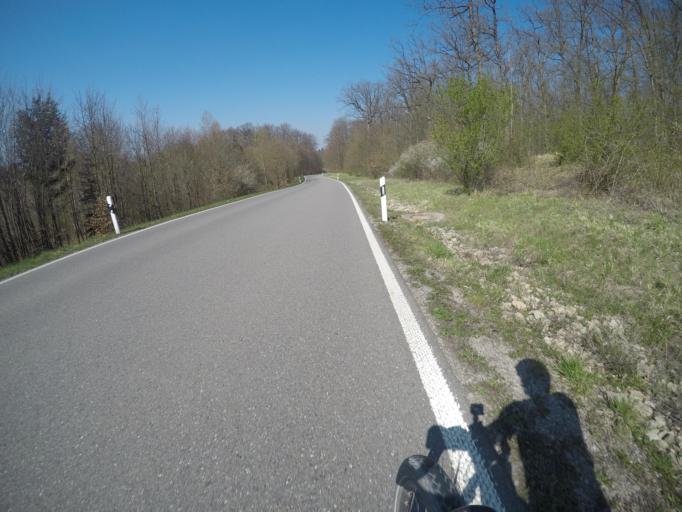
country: DE
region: Baden-Wuerttemberg
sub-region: Regierungsbezirk Stuttgart
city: Leonberg
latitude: 48.7610
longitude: 9.0087
